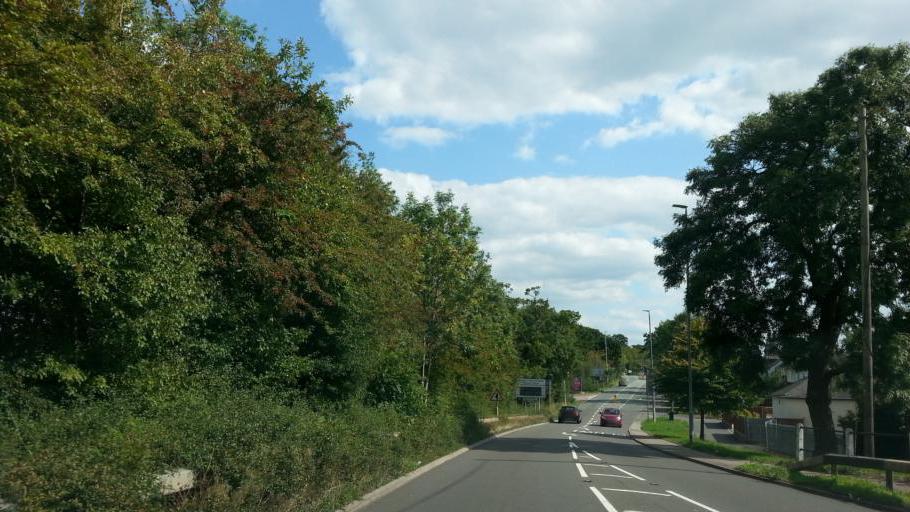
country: GB
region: England
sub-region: Leicestershire
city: Glenfield
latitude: 52.6286
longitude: -1.2049
